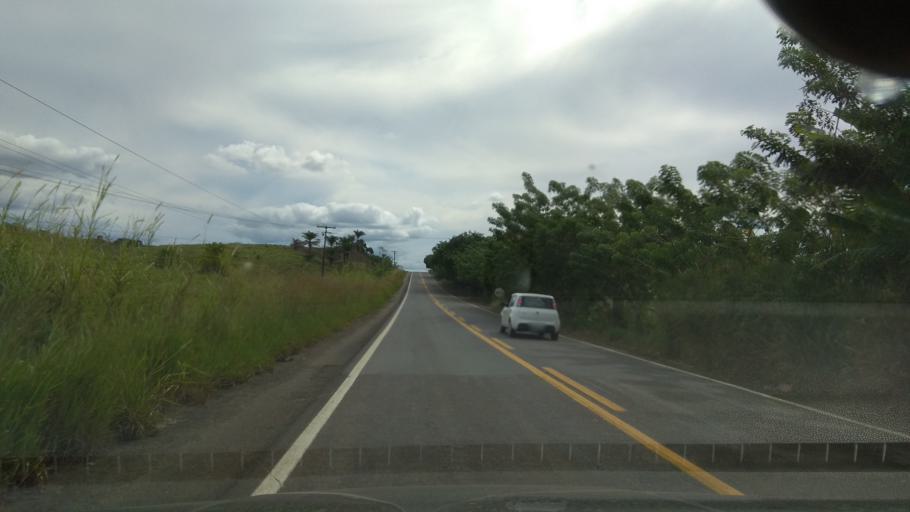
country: BR
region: Bahia
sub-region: Ubata
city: Ubata
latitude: -14.1969
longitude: -39.6215
